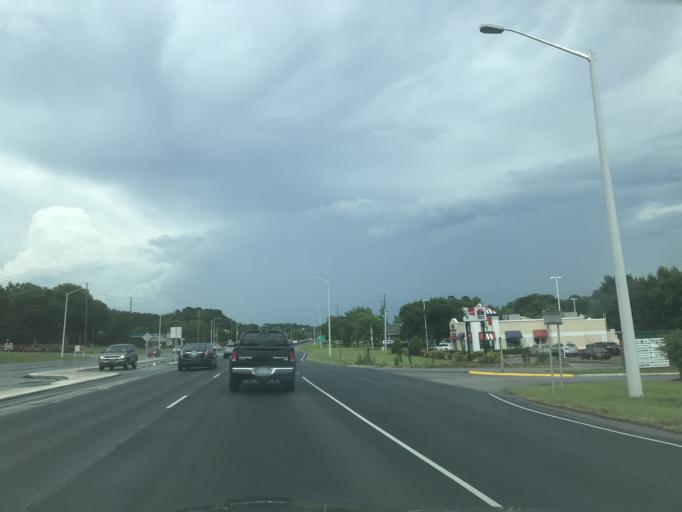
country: US
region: North Carolina
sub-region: Johnston County
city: Clayton
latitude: 35.6550
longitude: -78.4752
